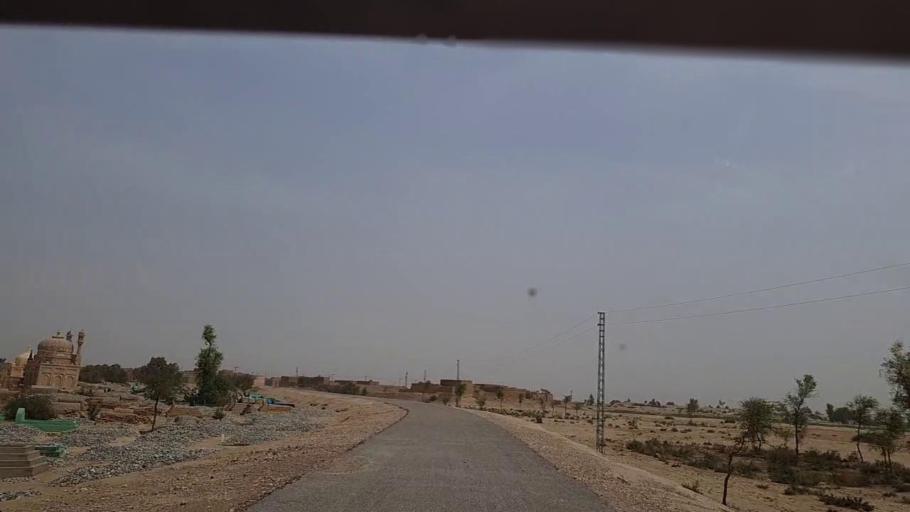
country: PK
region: Sindh
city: Phulji
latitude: 26.9993
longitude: 67.5032
